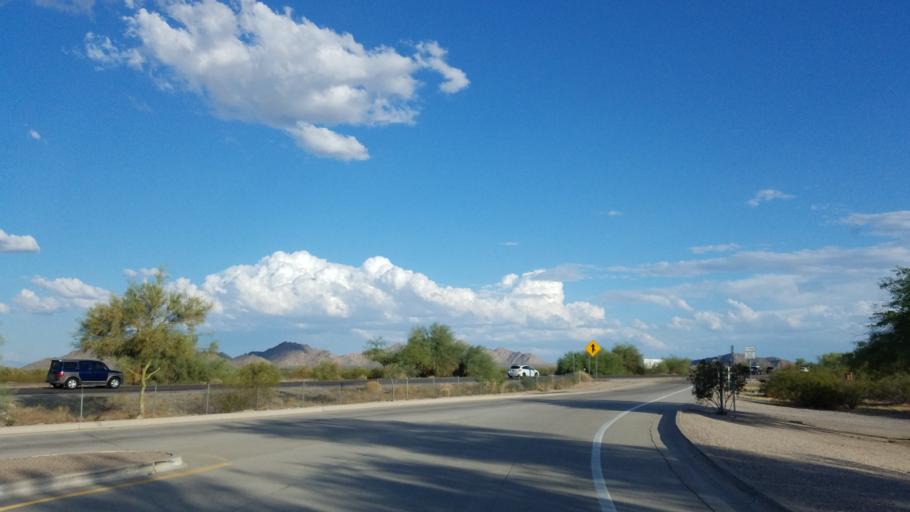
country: US
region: Arizona
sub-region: Pinal County
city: Sacaton
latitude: 33.0414
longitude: -111.7839
